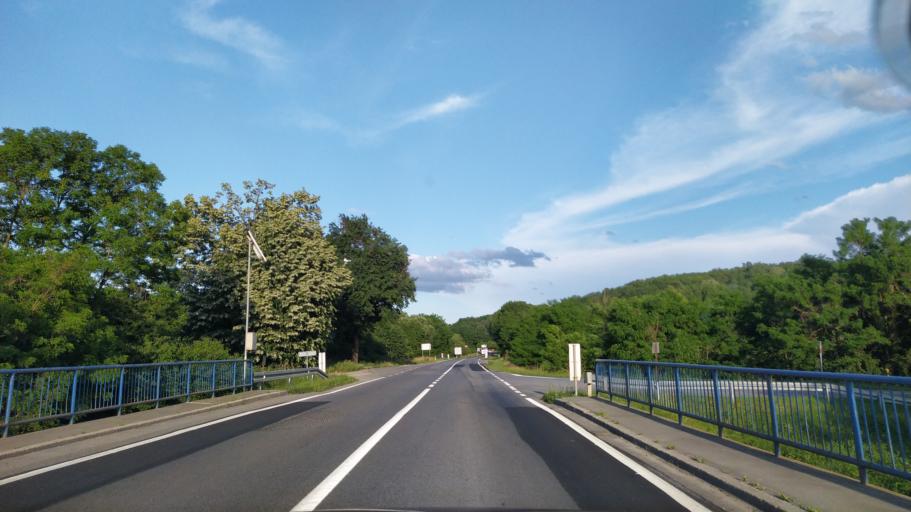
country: HR
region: Virovitick-Podravska
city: Cacinci
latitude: 45.6011
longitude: 17.8344
